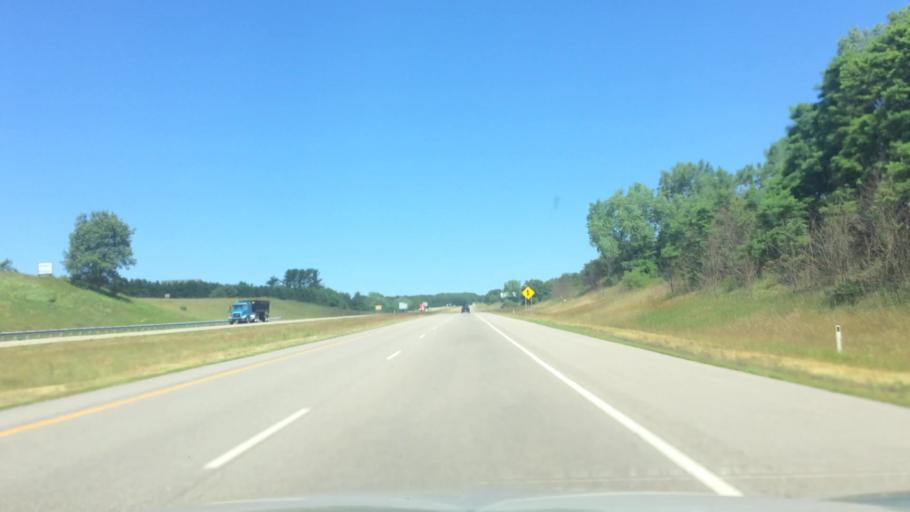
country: US
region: Wisconsin
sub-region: Marquette County
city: Westfield
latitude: 44.0352
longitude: -89.5287
